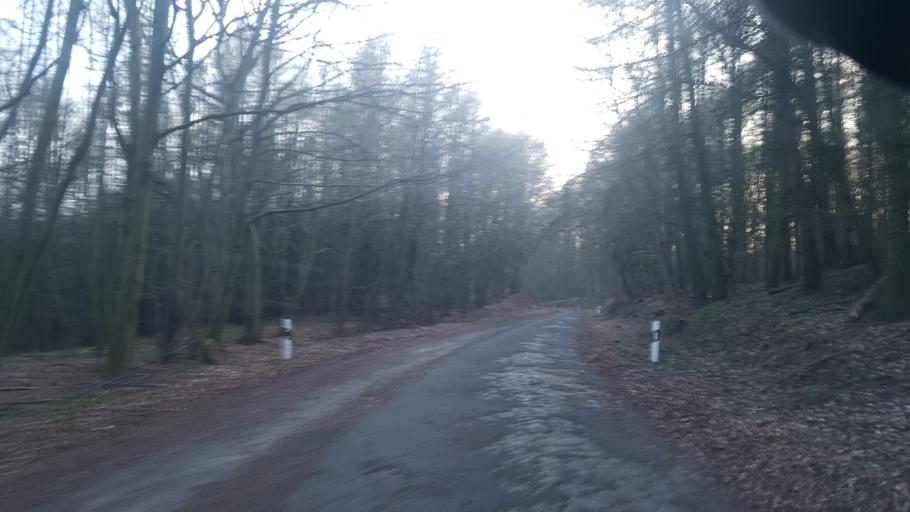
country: DE
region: Brandenburg
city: Gramzow
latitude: 53.1909
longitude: 13.9204
